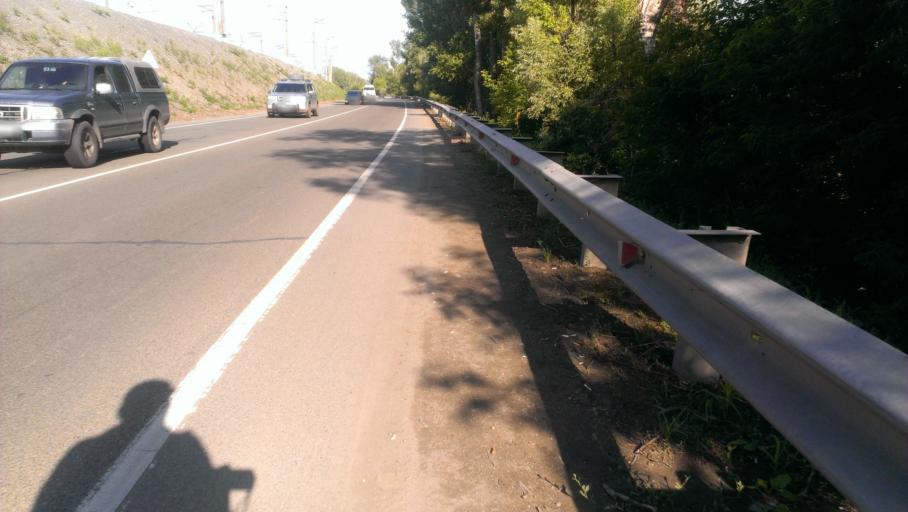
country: RU
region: Altai Krai
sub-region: Gorod Barnaulskiy
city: Barnaul
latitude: 53.3671
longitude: 83.8375
